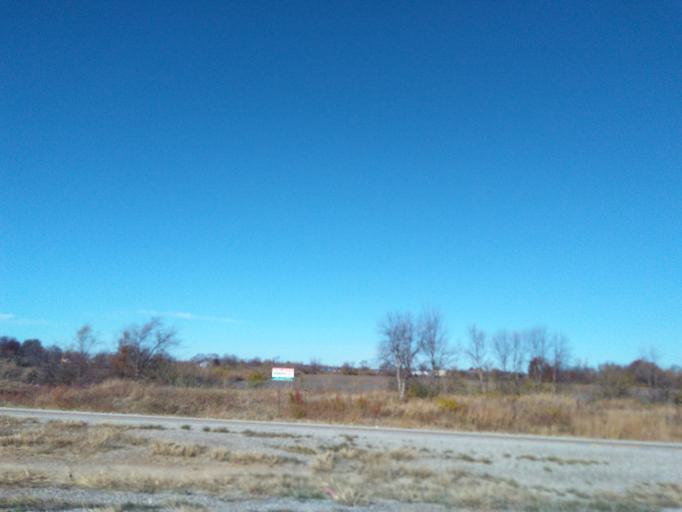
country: US
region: Illinois
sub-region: Saint Clair County
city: Dupo
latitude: 38.5325
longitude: -90.1938
